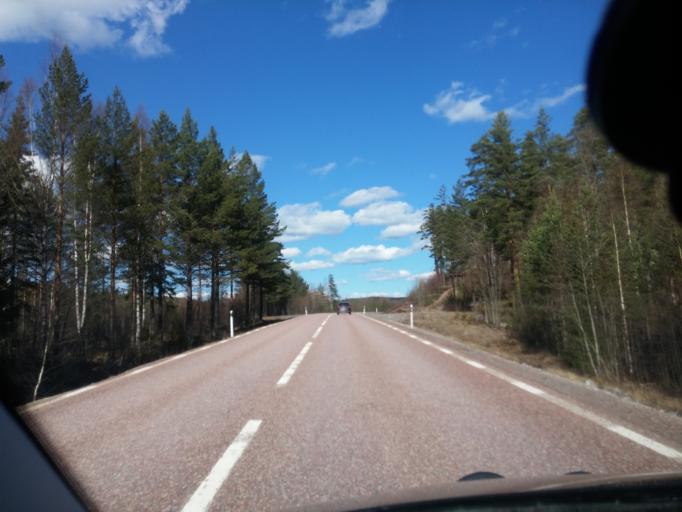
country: SE
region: Dalarna
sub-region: Faluns Kommun
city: Svardsjo
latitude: 60.7329
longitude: 15.7642
